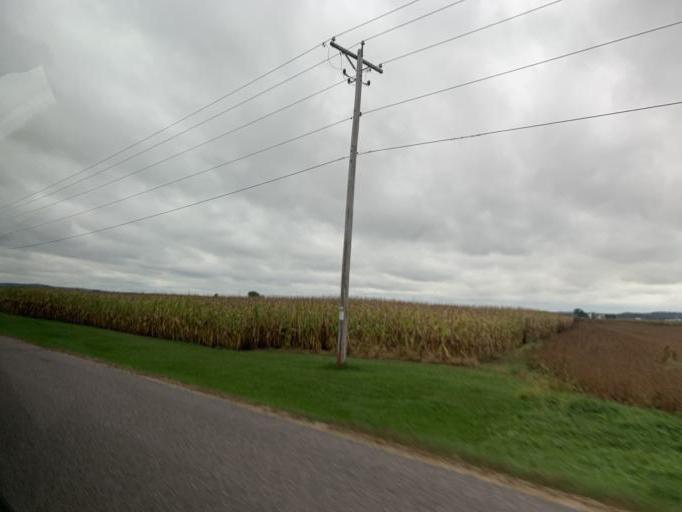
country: US
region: Wisconsin
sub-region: Sauk County
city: Prairie du Sac
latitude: 43.3183
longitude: -89.7753
